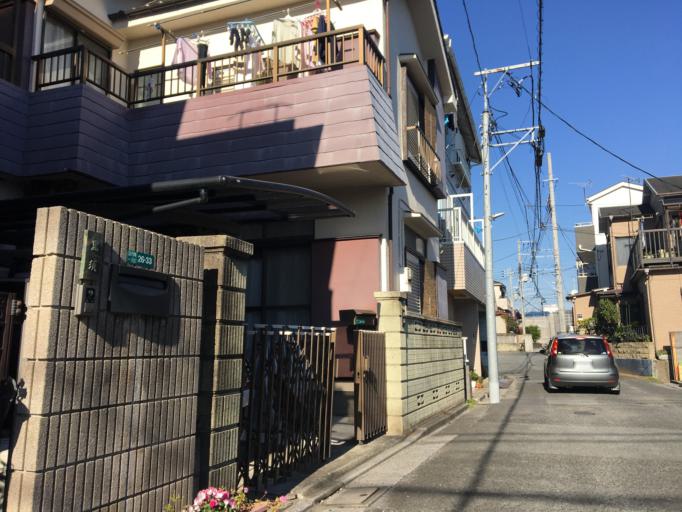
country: JP
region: Tokyo
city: Urayasu
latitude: 35.6868
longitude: 139.9079
